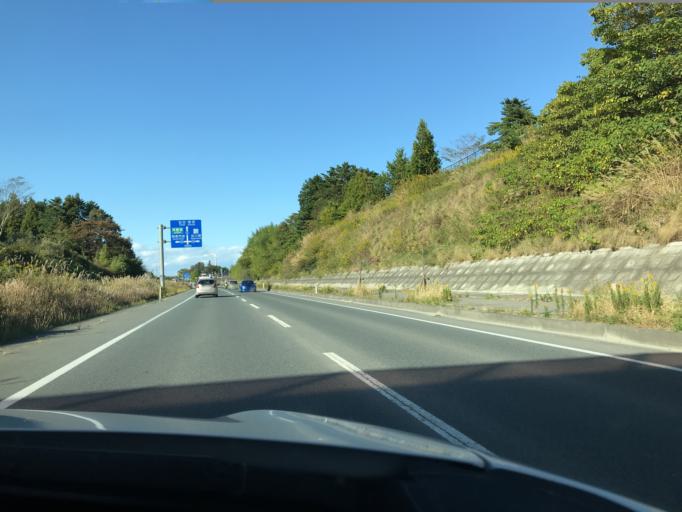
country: JP
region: Miyagi
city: Marumori
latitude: 37.8145
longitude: 140.9432
